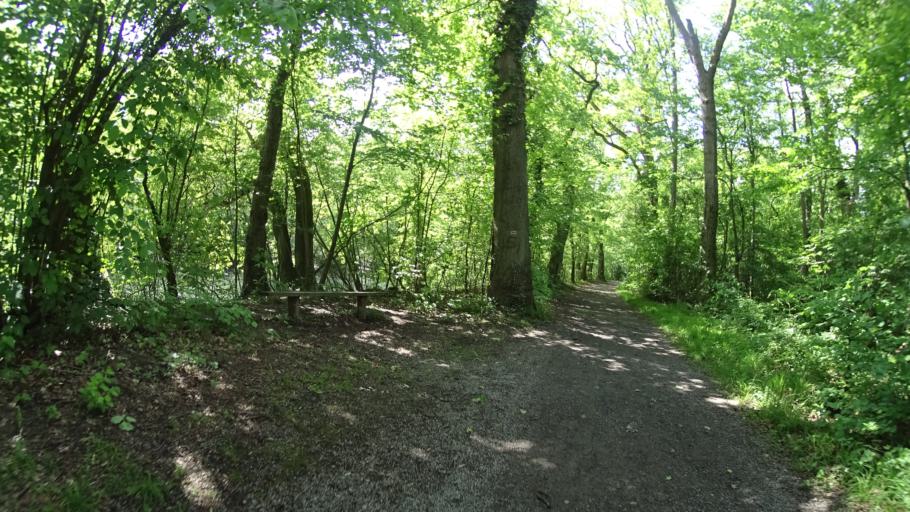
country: DE
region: Baden-Wuerttemberg
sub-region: Karlsruhe Region
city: Rheinstetten
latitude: 48.9956
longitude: 8.2960
